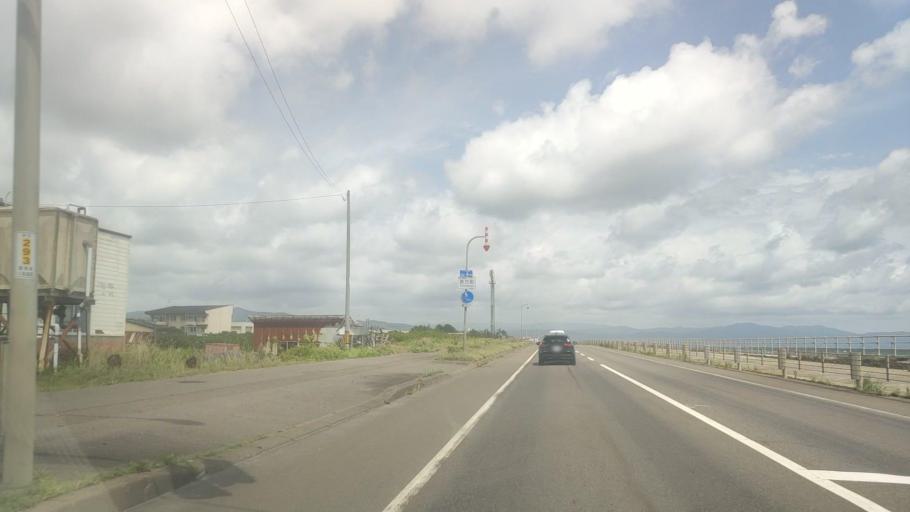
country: JP
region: Hokkaido
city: Niseko Town
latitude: 42.5026
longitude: 140.3711
